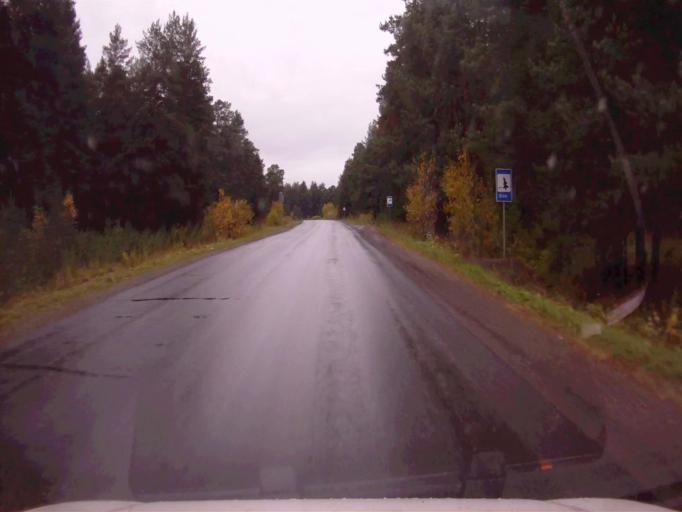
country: RU
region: Chelyabinsk
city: Verkhniy Ufaley
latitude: 56.0536
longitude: 60.1700
